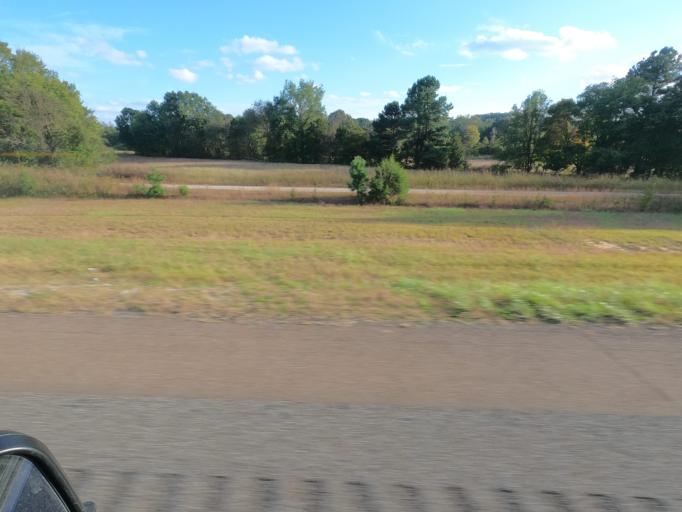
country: US
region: Tennessee
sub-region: Henderson County
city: Lexington
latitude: 35.7723
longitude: -88.4409
